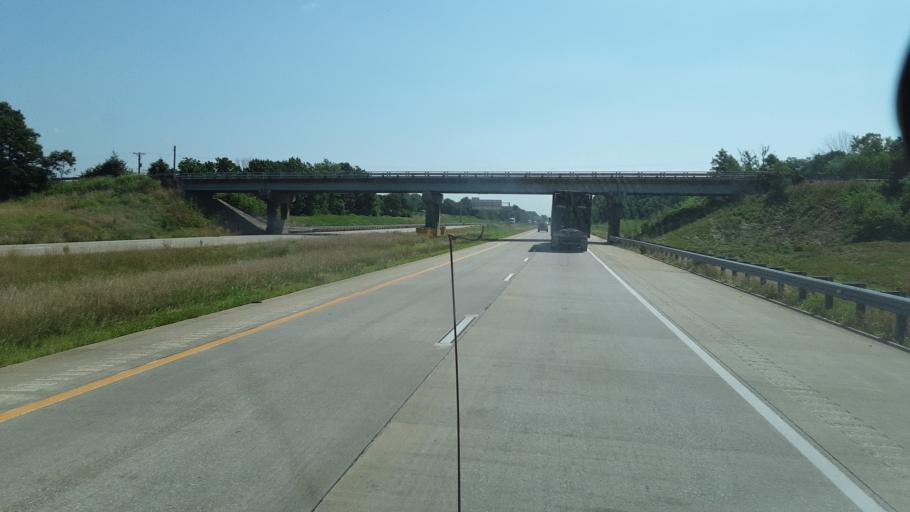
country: US
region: Illinois
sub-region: Effingham County
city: Teutopolis
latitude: 39.1508
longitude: -88.4963
